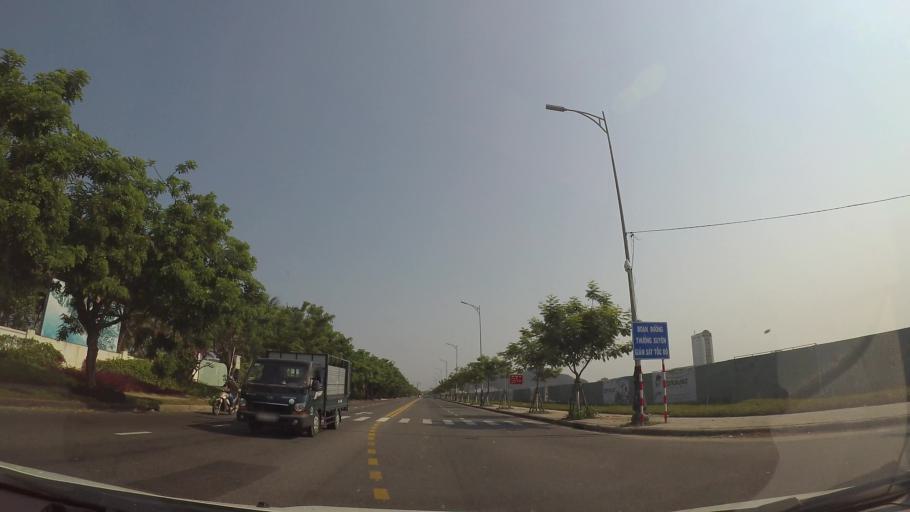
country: VN
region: Da Nang
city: Ngu Hanh Son
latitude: 16.0180
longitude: 108.2597
